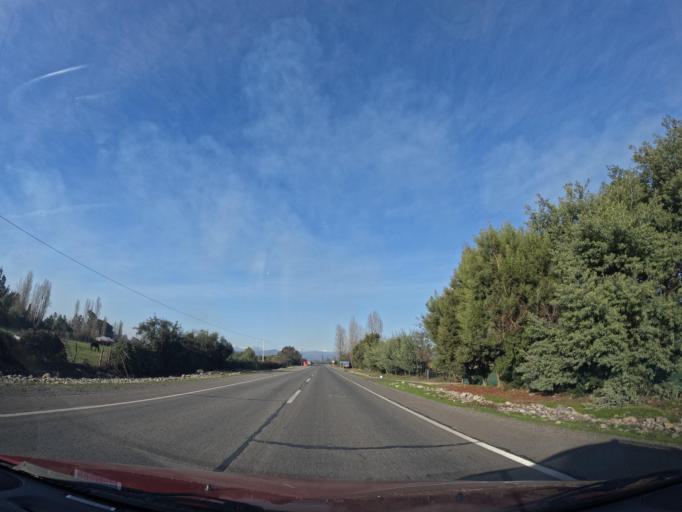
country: CL
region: Maule
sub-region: Provincia de Linares
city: Colbun
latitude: -35.6280
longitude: -71.4549
